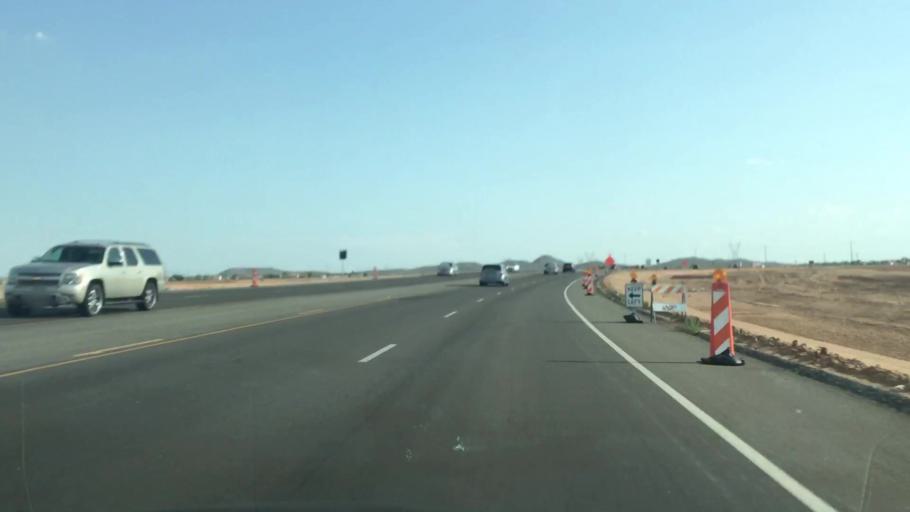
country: US
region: Arizona
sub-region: Pinal County
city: San Tan Valley
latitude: 33.1531
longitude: -111.5445
